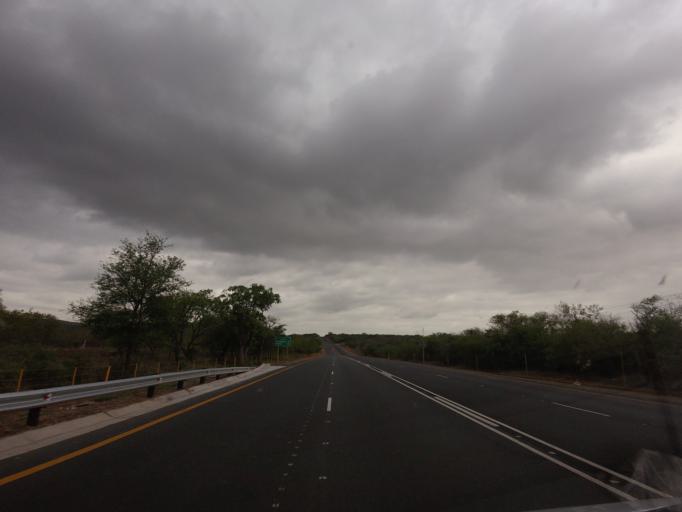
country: ZA
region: Mpumalanga
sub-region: Ehlanzeni District
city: Komatipoort
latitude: -25.4402
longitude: 31.7620
